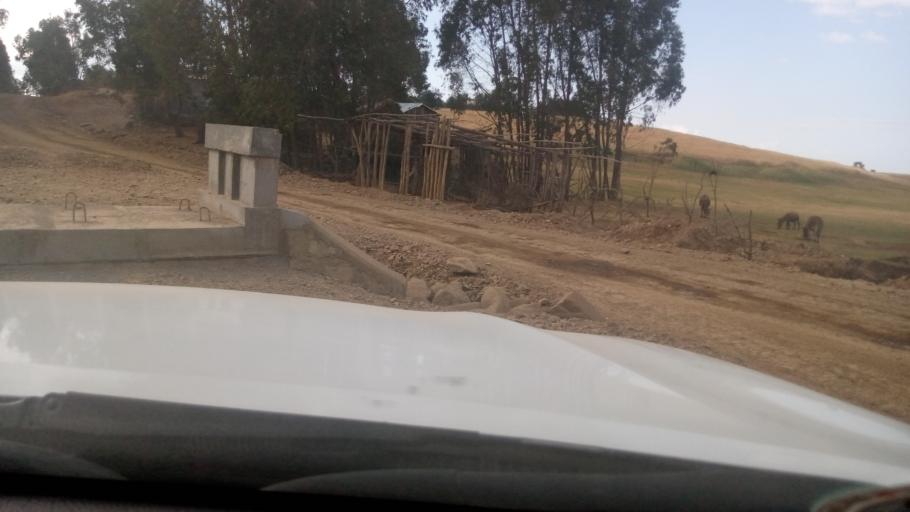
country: ET
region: Amhara
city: Debark'
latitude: 13.1568
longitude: 37.8258
